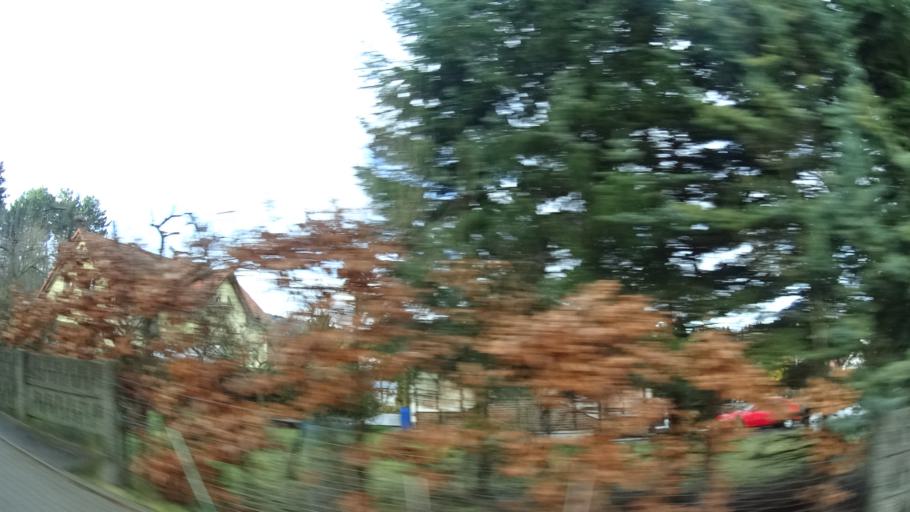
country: DE
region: Thuringia
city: Crawinkel
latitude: 50.7756
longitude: 10.7780
